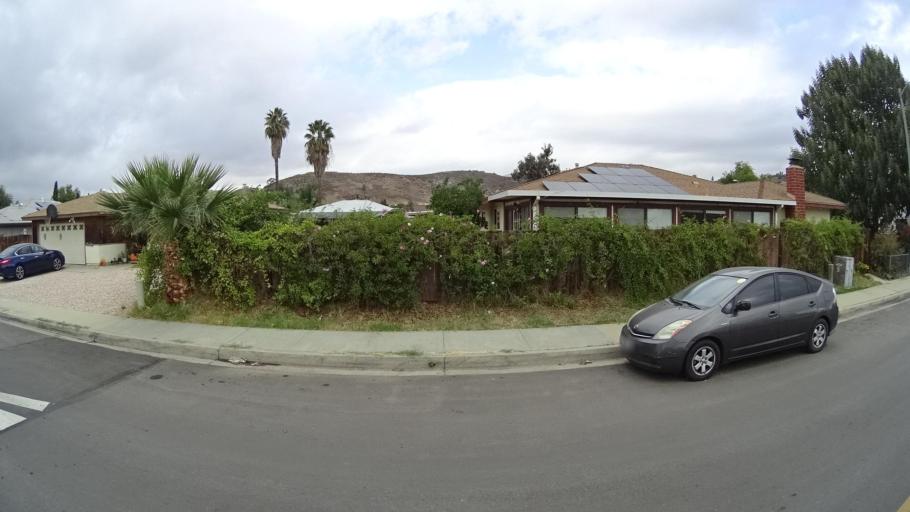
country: US
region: California
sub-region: San Diego County
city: Lakeside
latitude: 32.8612
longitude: -116.9118
